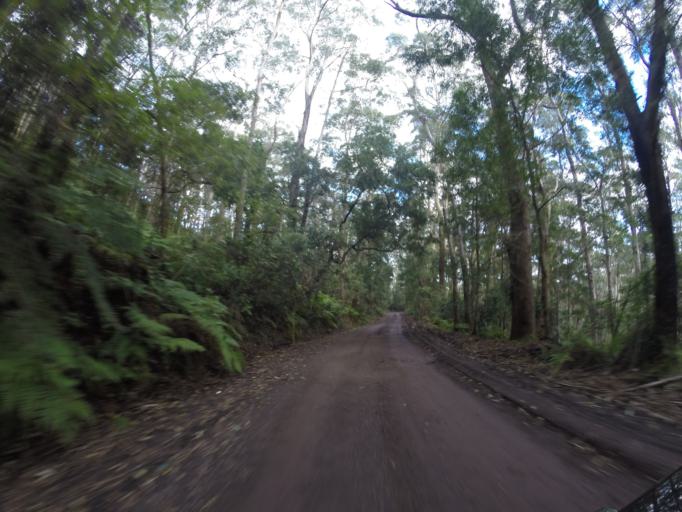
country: AU
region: New South Wales
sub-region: Wollongong
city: Cordeaux Heights
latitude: -34.4349
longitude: 150.7866
